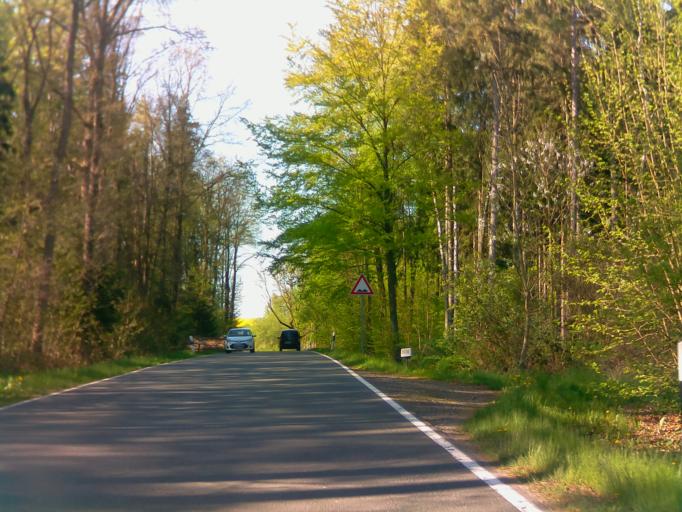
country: DE
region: Thuringia
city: Auma
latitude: 50.7083
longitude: 11.8909
